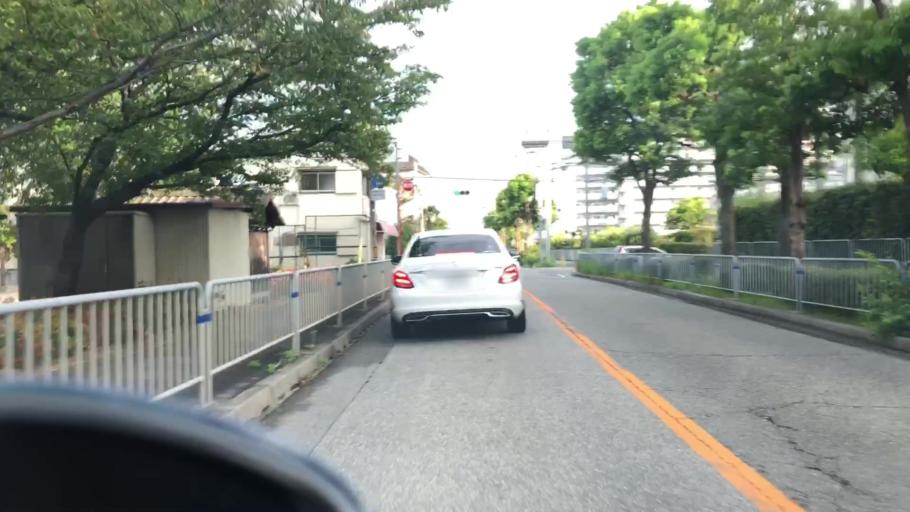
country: JP
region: Hyogo
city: Takarazuka
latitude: 34.7932
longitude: 135.3663
